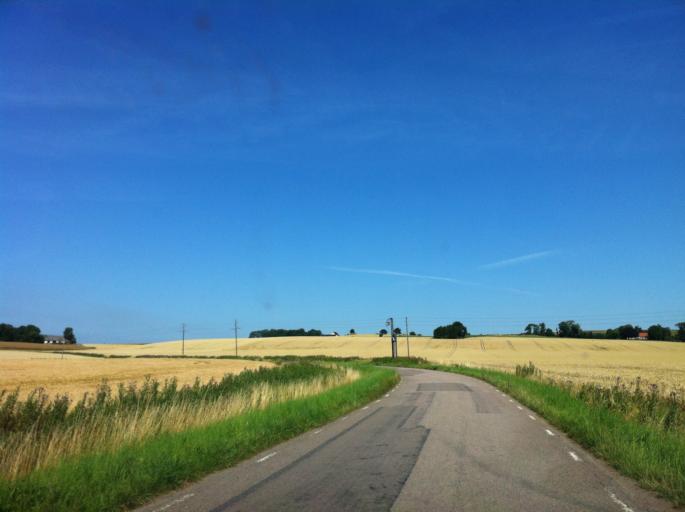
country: SE
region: Skane
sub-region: Landskrona
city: Asmundtorp
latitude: 55.8916
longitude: 12.9409
